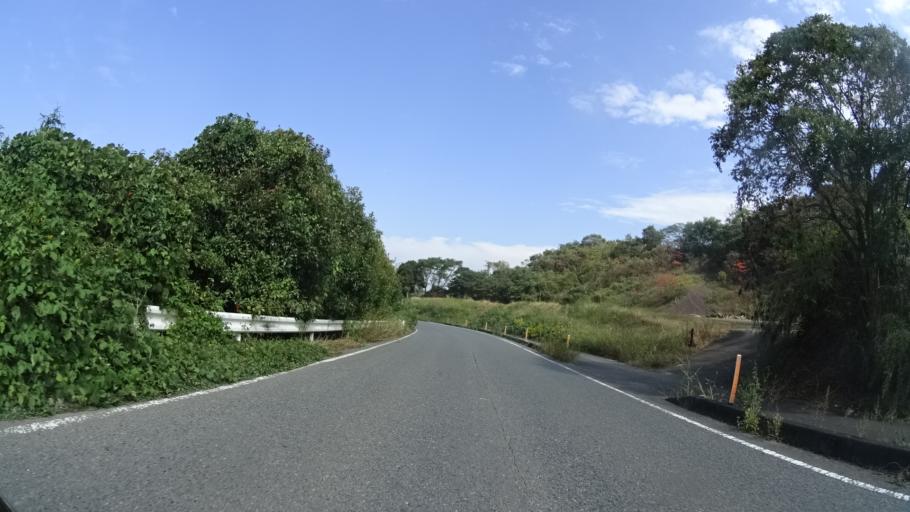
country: JP
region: Kumamoto
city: Uto
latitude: 32.6725
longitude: 130.7203
